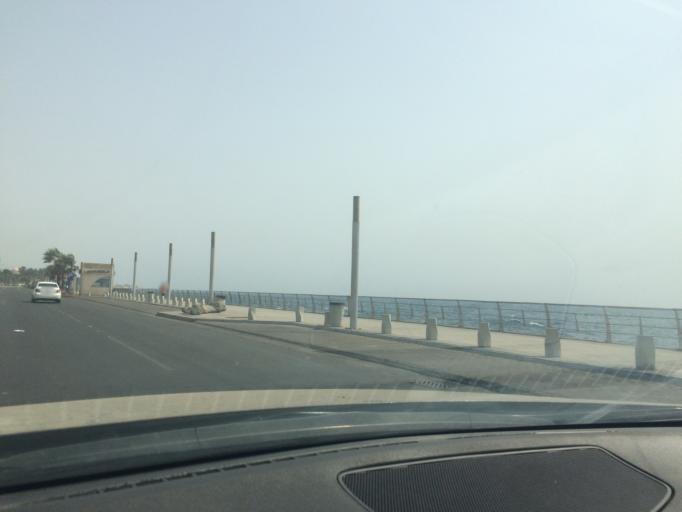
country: SA
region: Makkah
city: Jeddah
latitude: 21.5687
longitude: 39.1098
